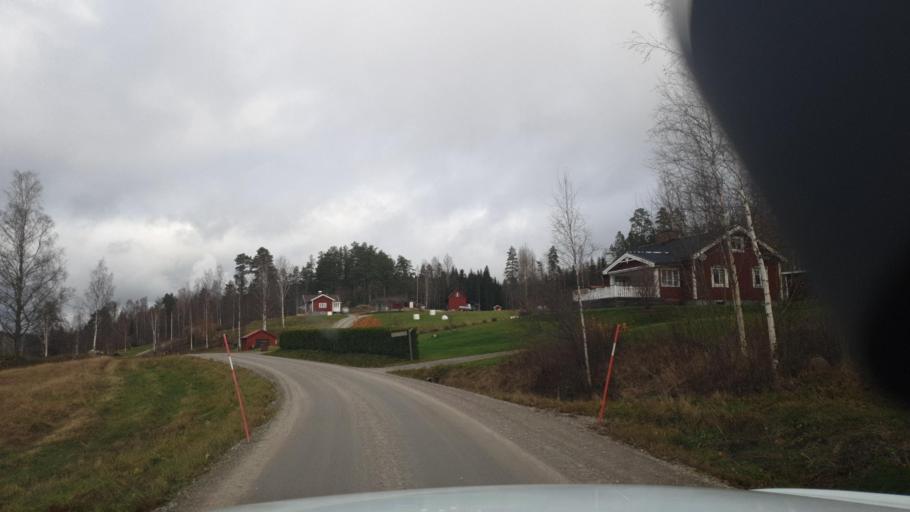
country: SE
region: Vaermland
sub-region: Arvika Kommun
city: Arvika
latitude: 59.7222
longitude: 12.8374
